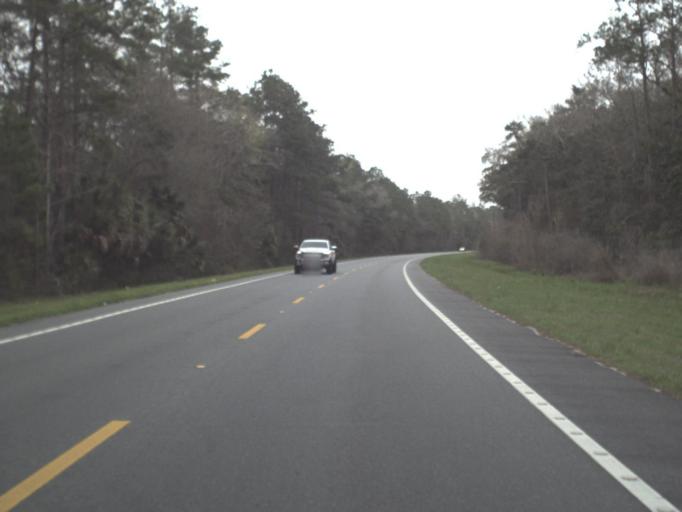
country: US
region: Florida
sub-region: Leon County
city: Woodville
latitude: 30.1820
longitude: -84.2407
